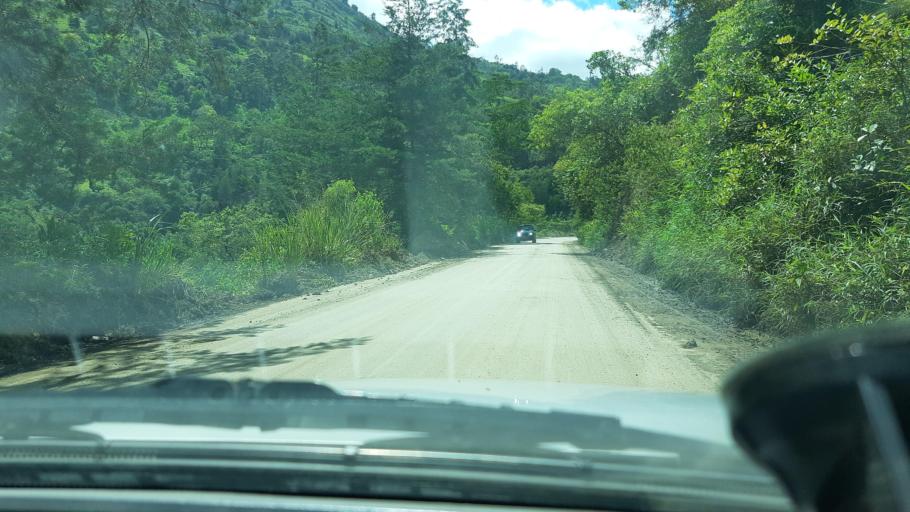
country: CO
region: Boyaca
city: Chinavita
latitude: 5.1814
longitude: -73.3833
